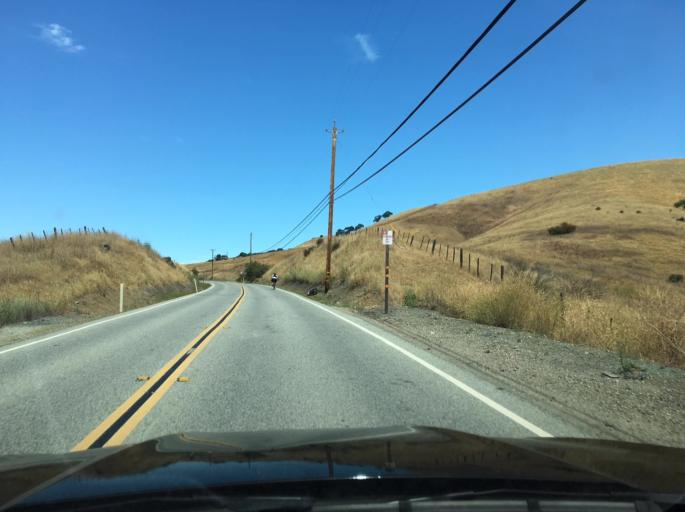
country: US
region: California
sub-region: Santa Clara County
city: Morgan Hill
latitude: 37.1837
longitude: -121.7634
